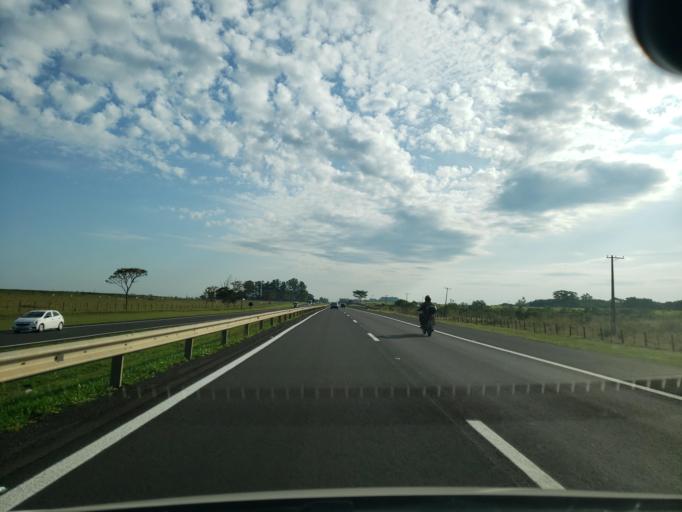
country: BR
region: Sao Paulo
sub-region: Guararapes
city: Guararapes
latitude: -21.2015
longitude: -50.5880
